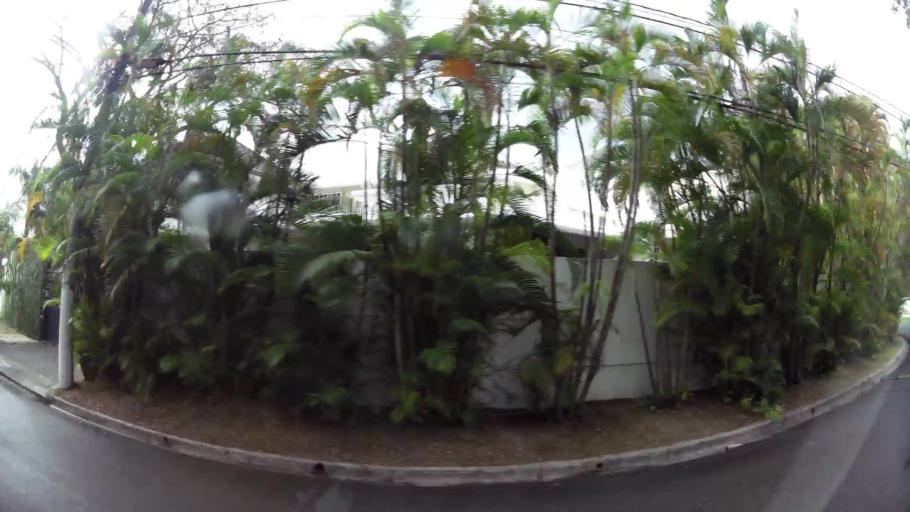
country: DO
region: Nacional
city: La Agustina
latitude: 18.5092
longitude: -69.9472
